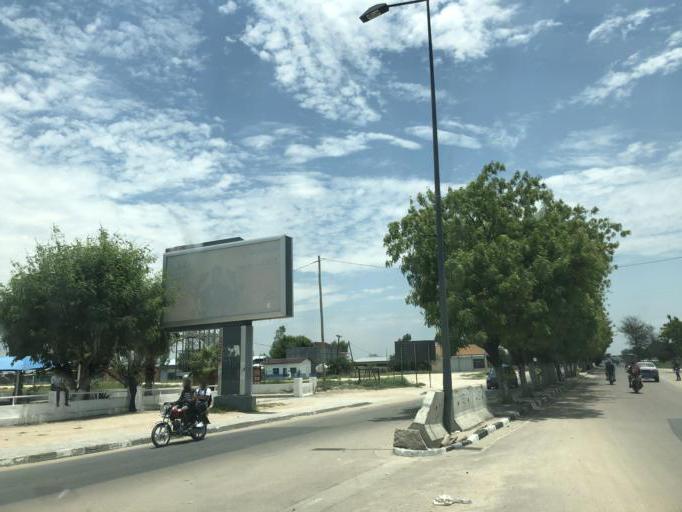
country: AO
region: Cunene
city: Ondjiva
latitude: -17.0684
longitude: 15.7218
